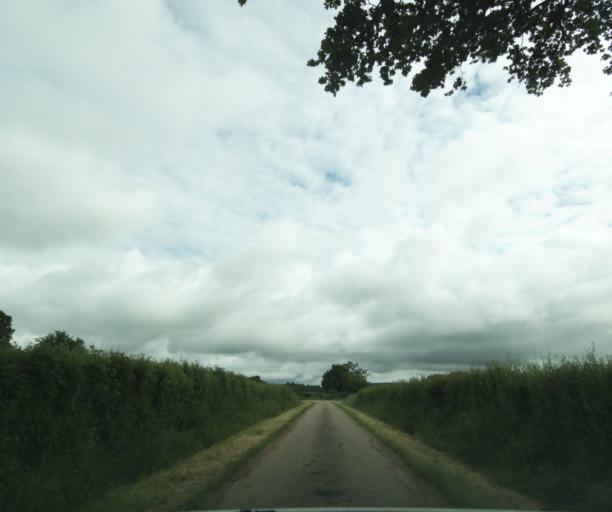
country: FR
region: Bourgogne
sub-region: Departement de Saone-et-Loire
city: Charolles
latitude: 46.4220
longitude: 4.3149
